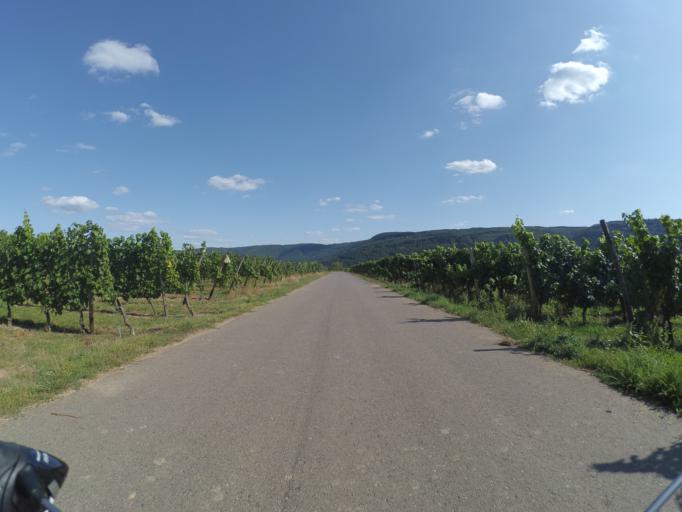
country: DE
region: Rheinland-Pfalz
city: Longuich
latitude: 49.8014
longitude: 6.8038
